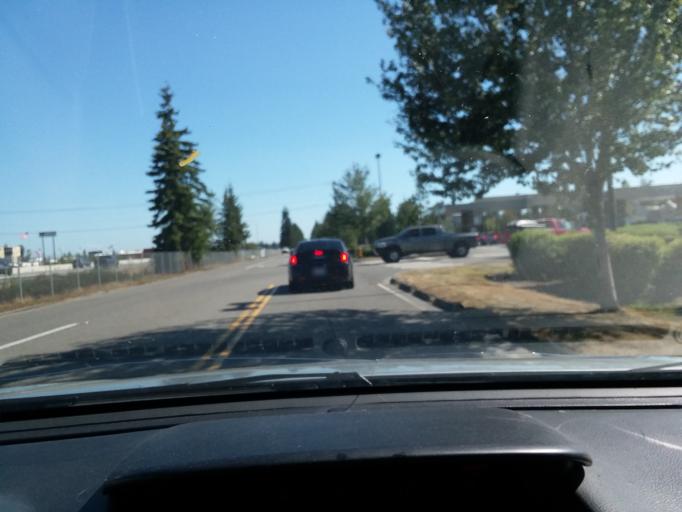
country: US
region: Washington
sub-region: Snohomish County
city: Smokey Point
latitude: 48.1480
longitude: -122.1888
